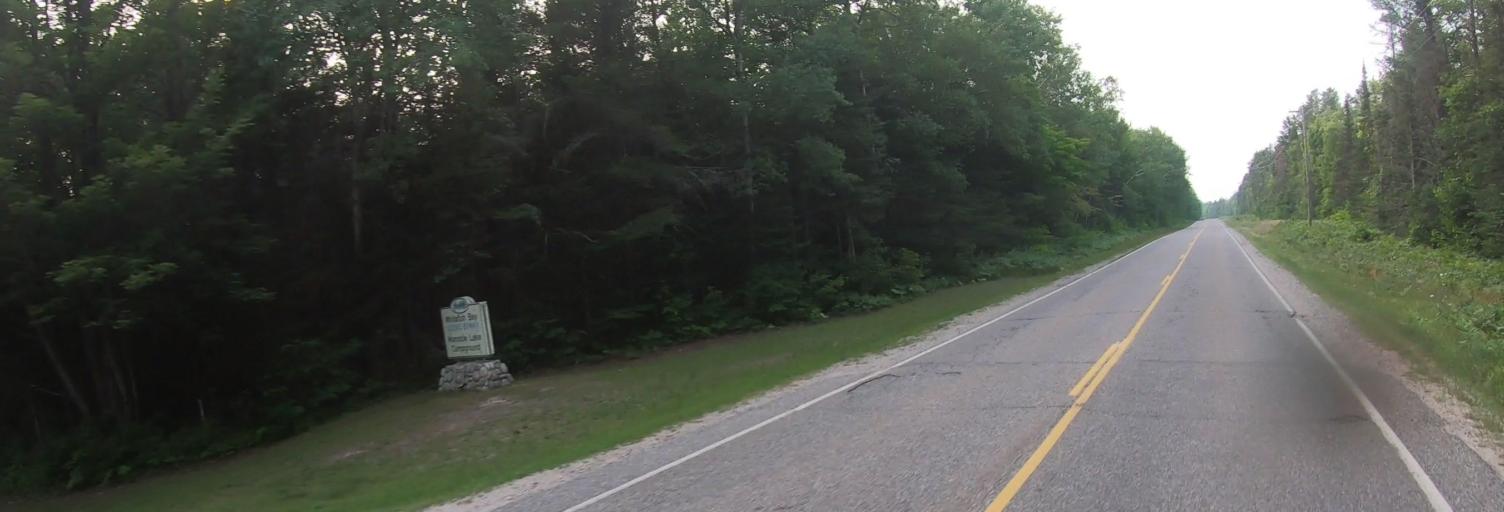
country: US
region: Michigan
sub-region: Chippewa County
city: Sault Ste. Marie
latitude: 46.4722
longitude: -84.6215
